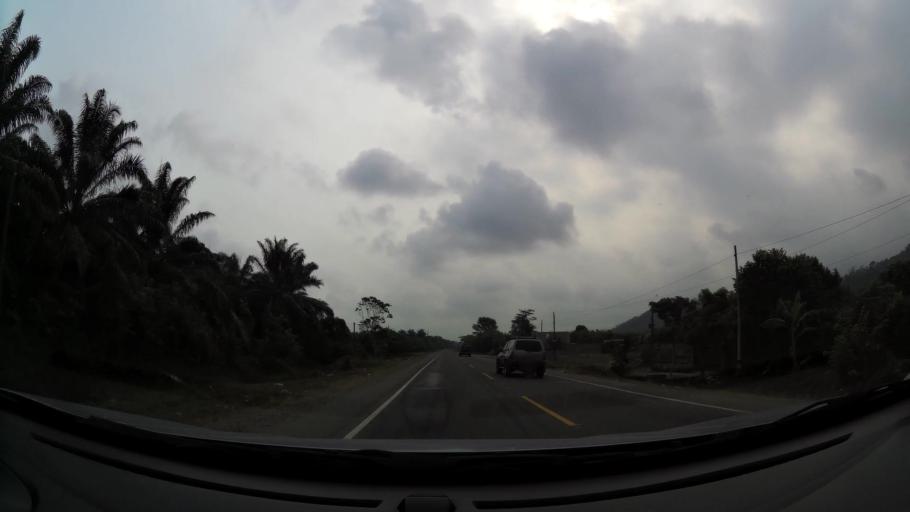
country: HN
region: Yoro
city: Guaimitas
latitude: 15.4890
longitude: -87.7567
